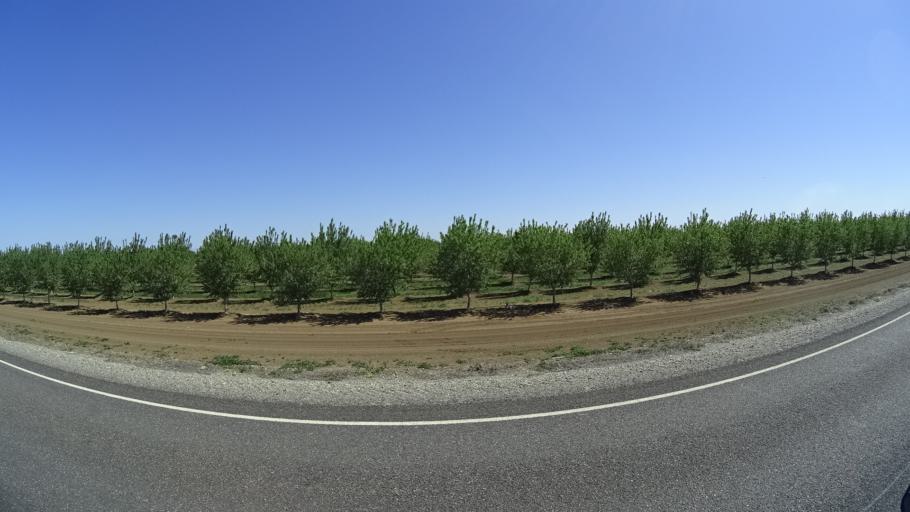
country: US
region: California
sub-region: Glenn County
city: Willows
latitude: 39.5779
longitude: -122.2496
